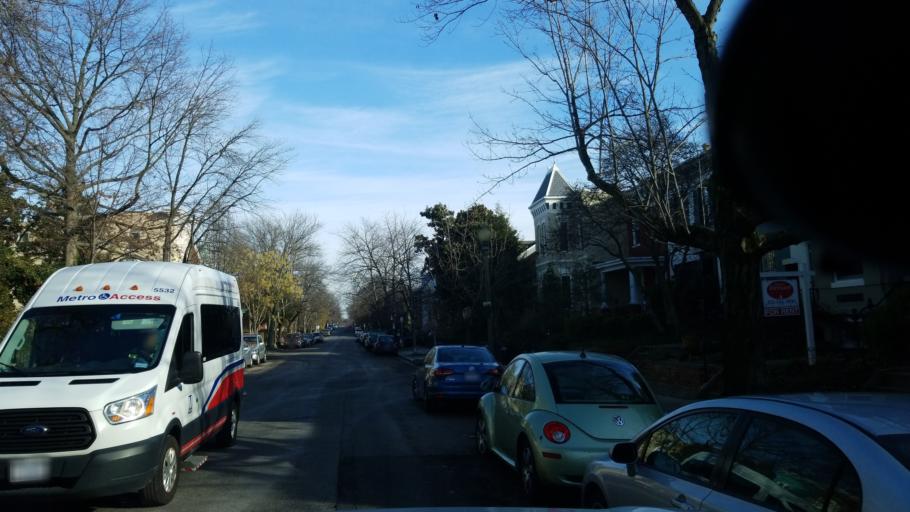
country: US
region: Washington, D.C.
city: Washington, D.C.
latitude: 38.8812
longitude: -76.9981
